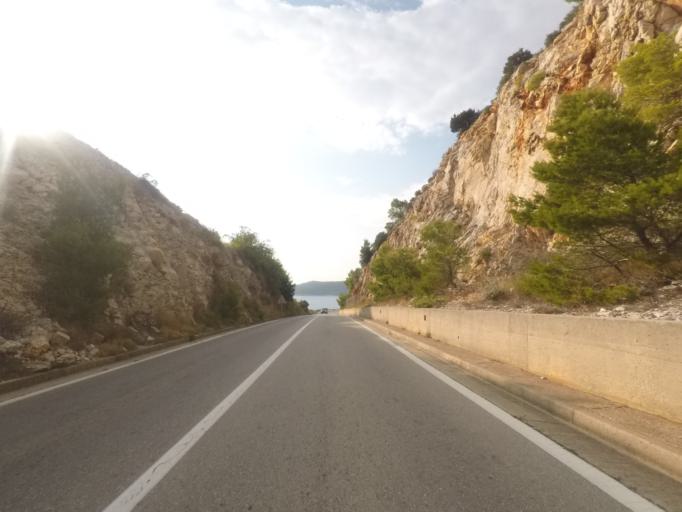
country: HR
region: Splitsko-Dalmatinska
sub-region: Grad Hvar
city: Hvar
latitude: 43.1529
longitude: 16.5131
